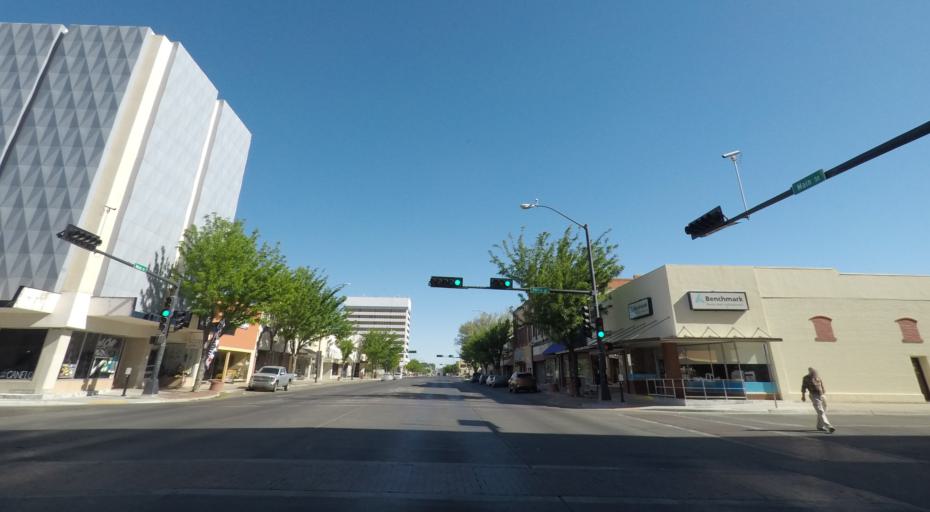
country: US
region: New Mexico
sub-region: Chaves County
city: Roswell
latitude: 33.3952
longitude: -104.5228
